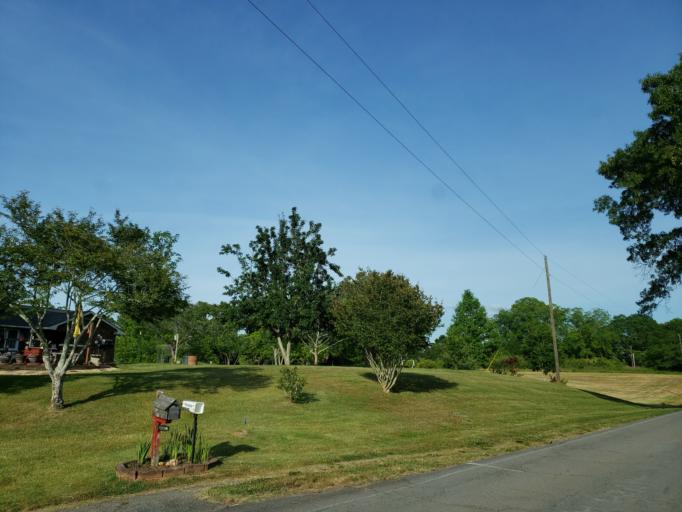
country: US
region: Georgia
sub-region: Carroll County
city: Bowdon
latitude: 33.4750
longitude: -85.3023
